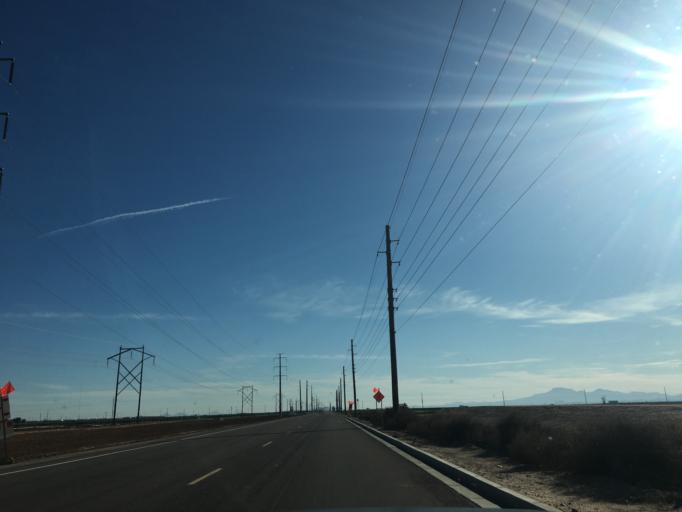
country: US
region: Arizona
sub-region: Pinal County
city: Maricopa
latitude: 33.0345
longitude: -111.9966
